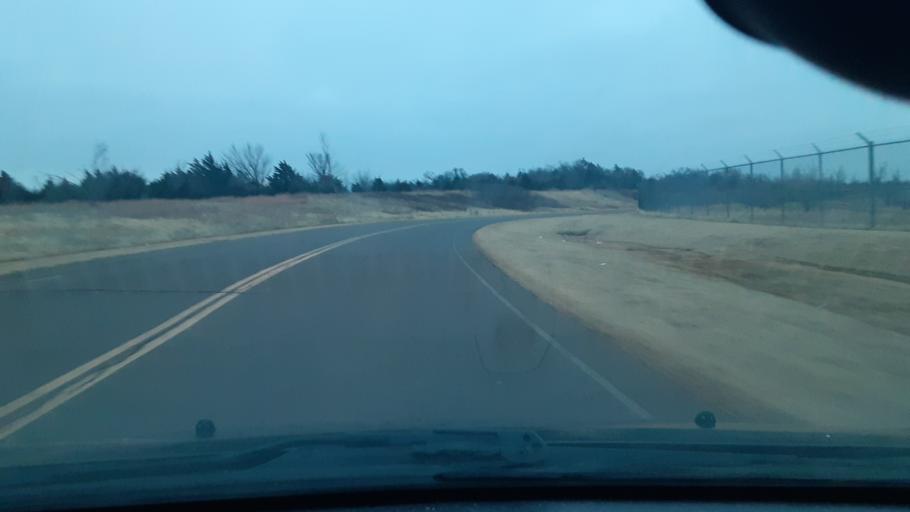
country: US
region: Oklahoma
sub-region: Logan County
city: Guthrie
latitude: 35.8617
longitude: -97.4170
